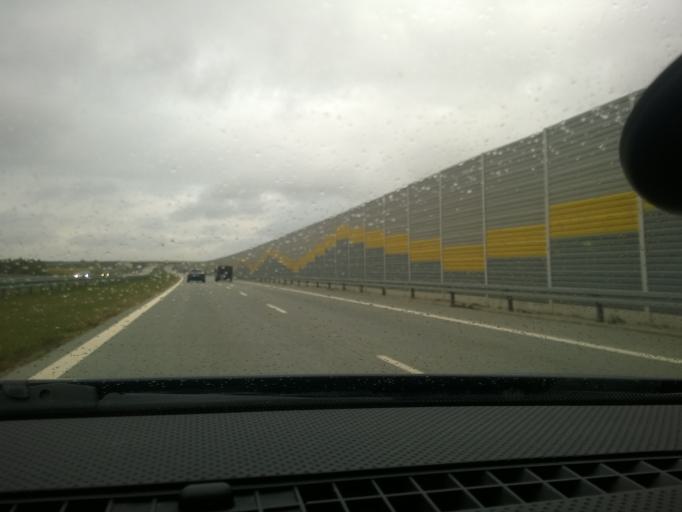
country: PL
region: Lodz Voivodeship
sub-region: Powiat laski
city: Lask
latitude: 51.5565
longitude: 19.1133
